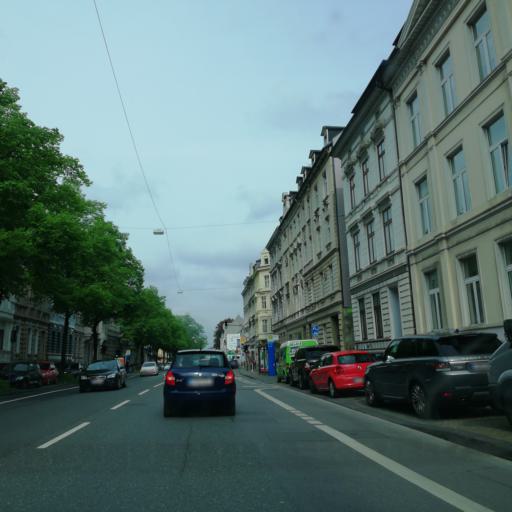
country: DE
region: North Rhine-Westphalia
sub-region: Regierungsbezirk Dusseldorf
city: Wuppertal
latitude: 51.2491
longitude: 7.1240
